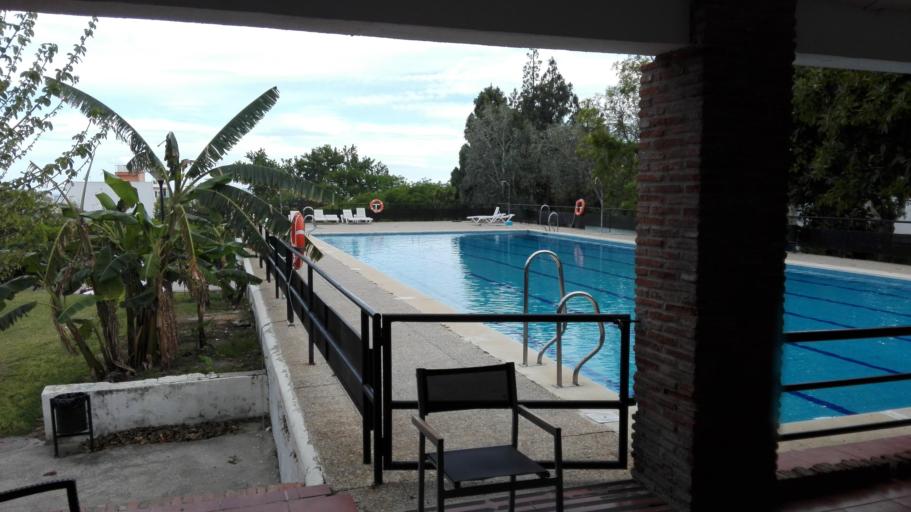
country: ES
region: Andalusia
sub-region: Provincia de Malaga
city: Marbella
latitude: 36.5212
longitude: -4.8876
